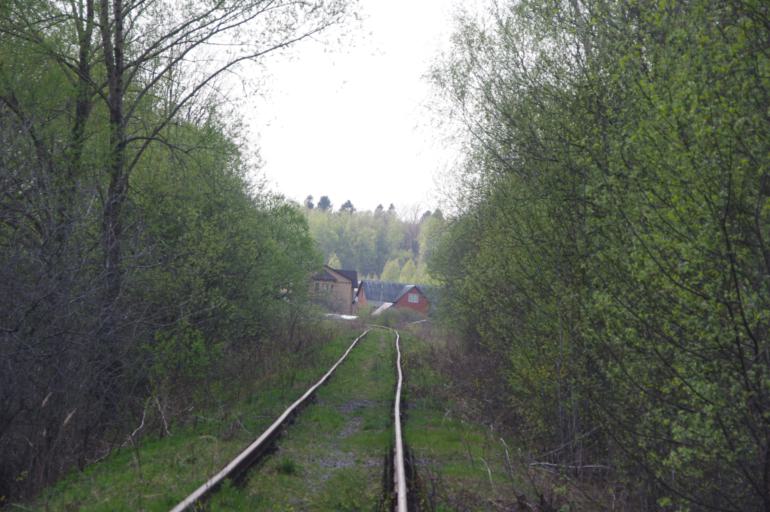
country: RU
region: Moskovskaya
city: Klin
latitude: 56.3322
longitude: 36.6639
